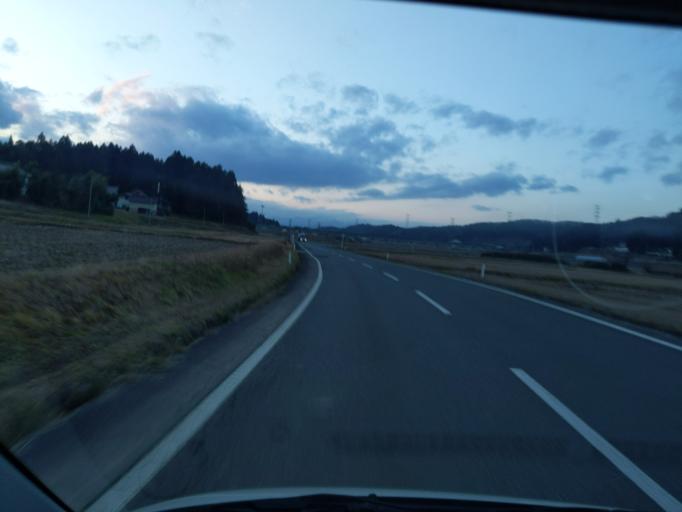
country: JP
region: Iwate
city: Ichinoseki
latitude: 38.8433
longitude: 141.1187
